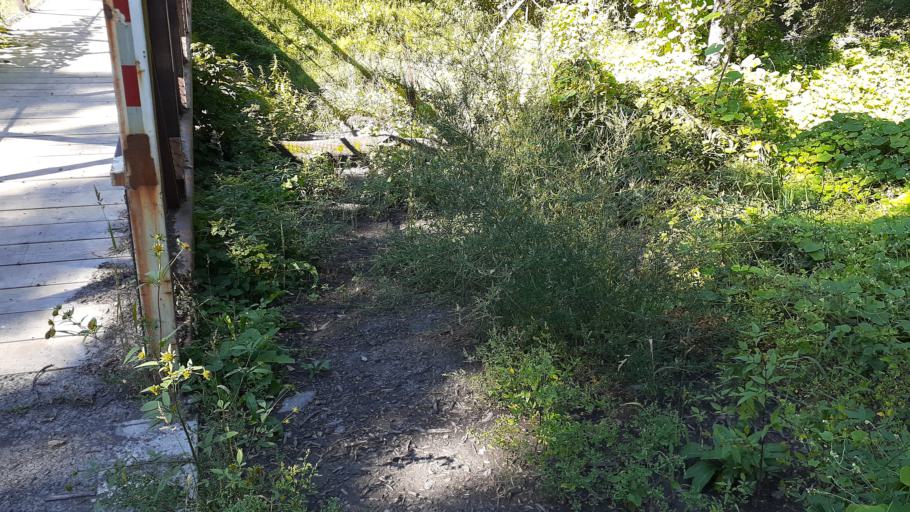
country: US
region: Minnesota
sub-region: Clay County
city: Oakport
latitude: 46.9098
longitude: -96.7610
